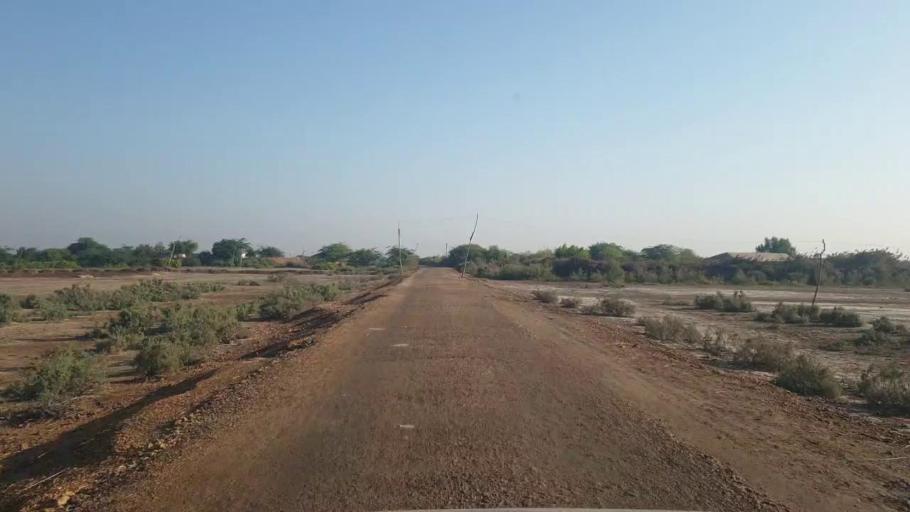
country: PK
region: Sindh
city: Badin
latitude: 24.7293
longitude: 68.8666
